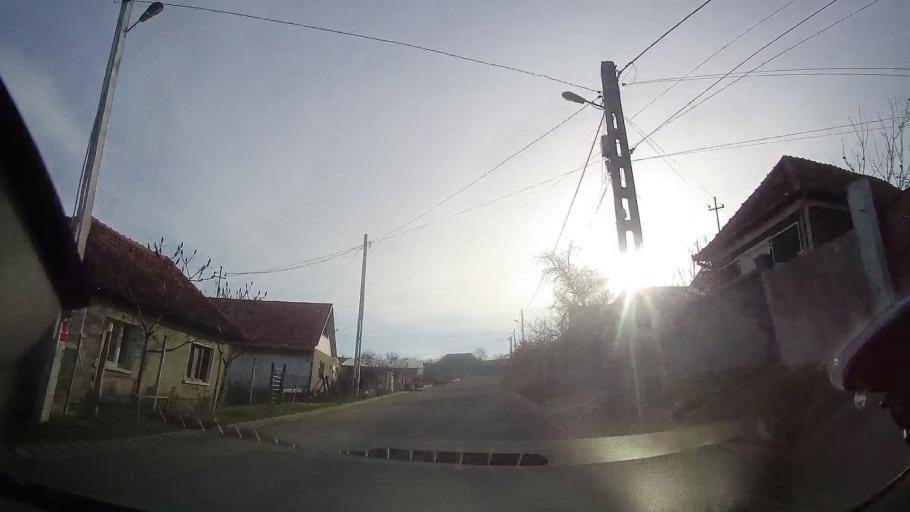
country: RO
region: Bihor
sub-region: Comuna Tileagd
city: Tileagd
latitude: 47.1021
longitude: 22.1753
